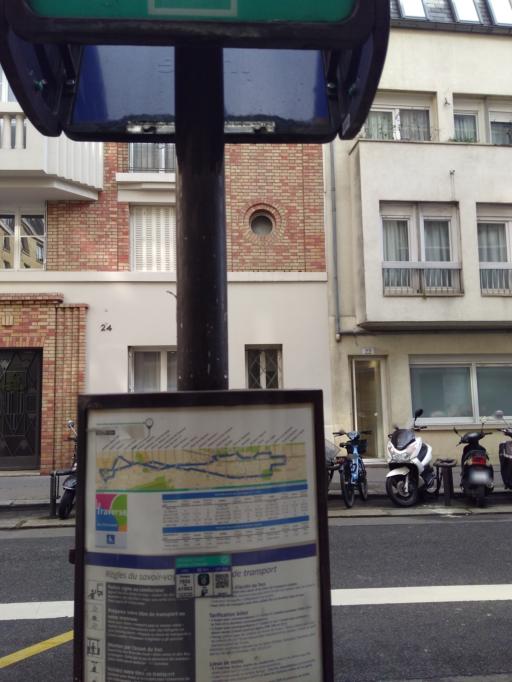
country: FR
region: Ile-de-France
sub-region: Departement de Seine-Saint-Denis
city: Bagnolet
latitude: 48.8632
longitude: 2.4043
